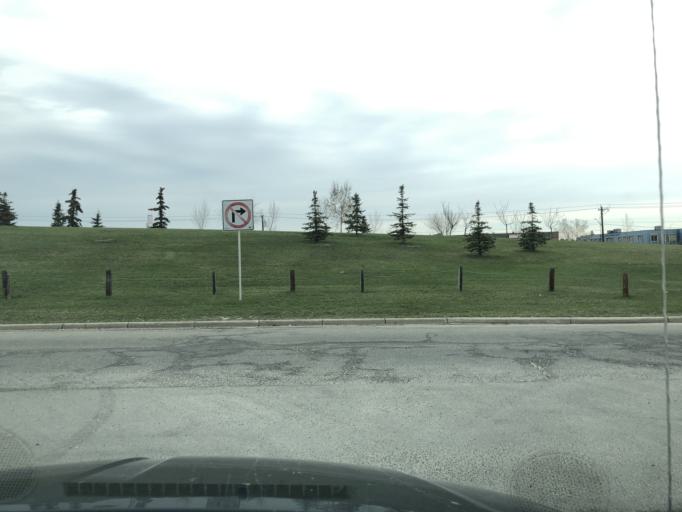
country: CA
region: Alberta
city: Calgary
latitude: 51.0741
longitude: -114.0101
